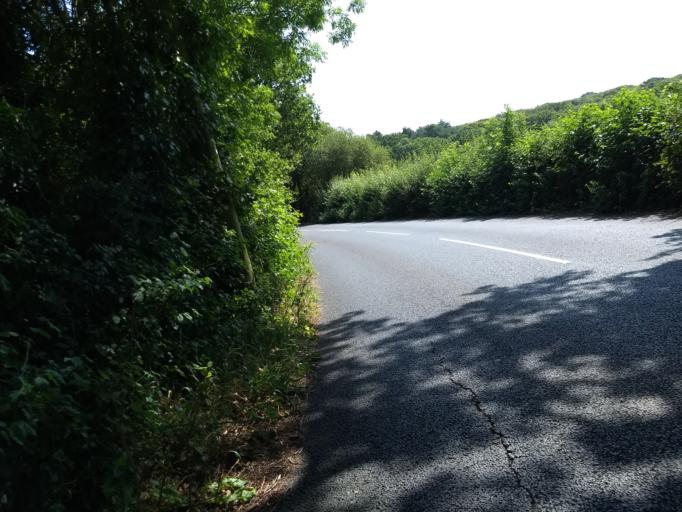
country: GB
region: England
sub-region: Isle of Wight
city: Northwood
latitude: 50.7303
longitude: -1.3307
